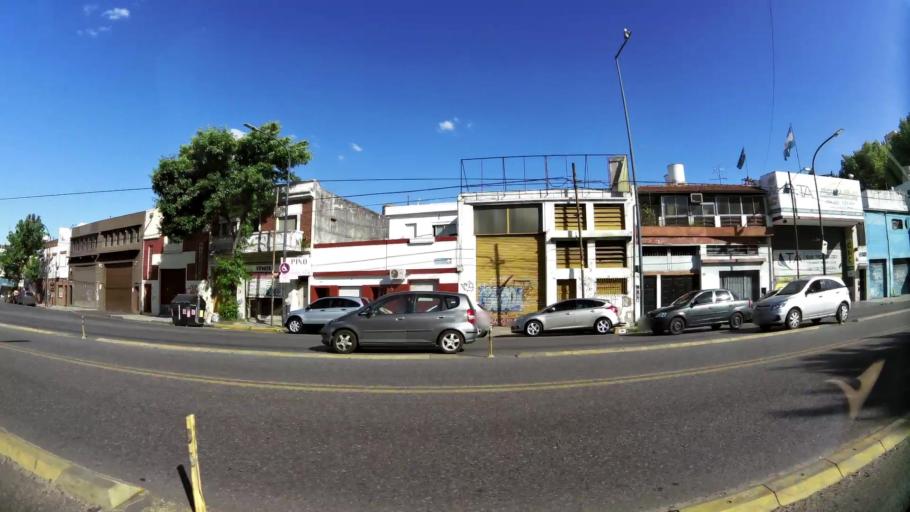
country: AR
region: Buenos Aires F.D.
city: Villa Santa Rita
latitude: -34.6157
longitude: -58.4736
